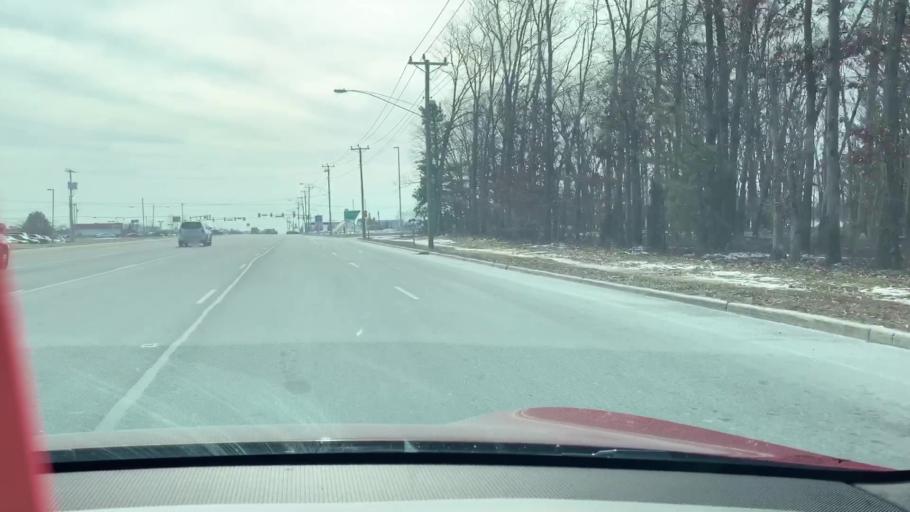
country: US
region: New Jersey
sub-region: Atlantic County
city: Northfield
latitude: 39.3965
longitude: -74.5604
